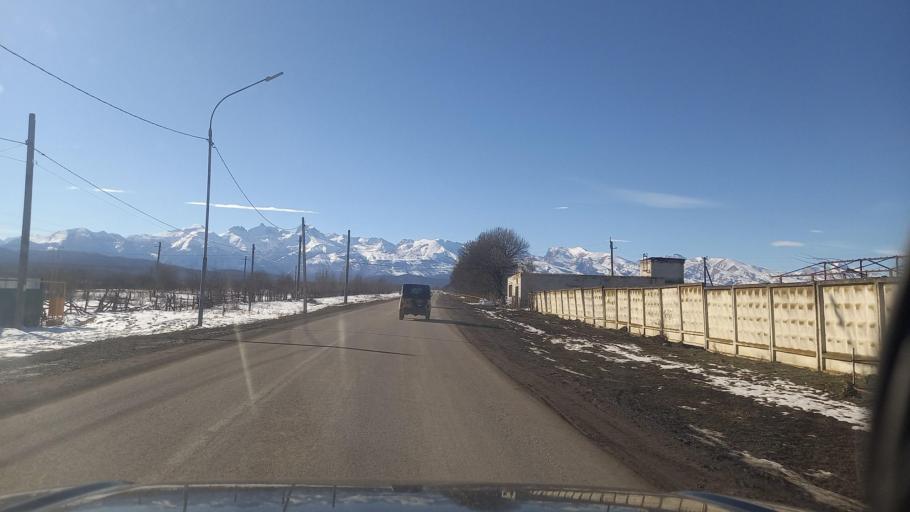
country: RU
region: North Ossetia
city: Chikola
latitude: 43.1853
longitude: 43.8985
